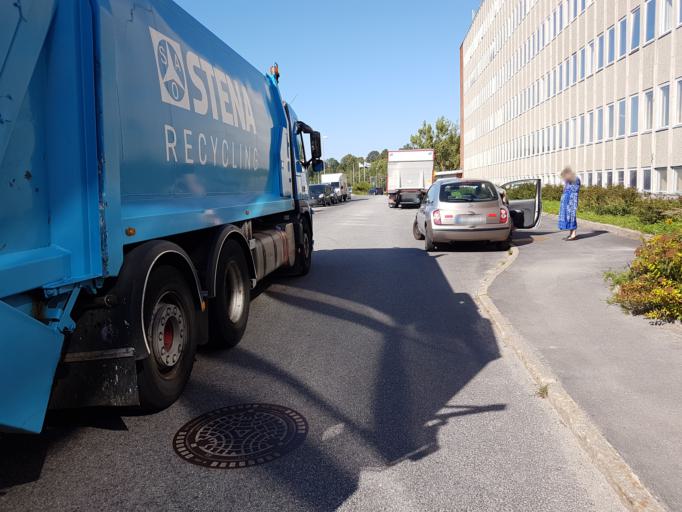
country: SE
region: Stockholm
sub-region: Huddinge Kommun
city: Huddinge
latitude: 59.2220
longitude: 17.9565
